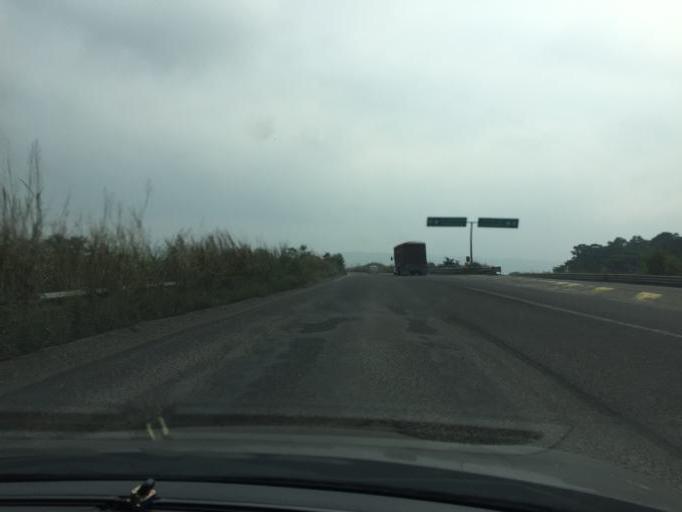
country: MX
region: Veracruz
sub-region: Moloacan
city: Tlacuilolapan
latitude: 18.0698
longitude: -94.2573
